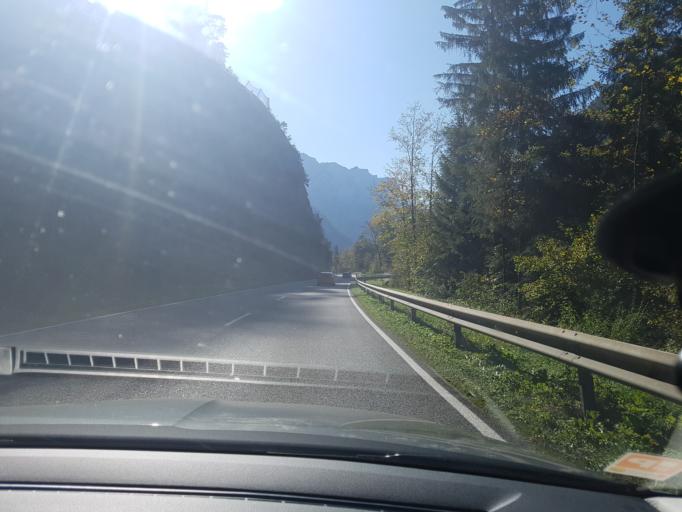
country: DE
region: Bavaria
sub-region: Upper Bavaria
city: Bad Reichenhall
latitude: 47.7015
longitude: 12.8526
